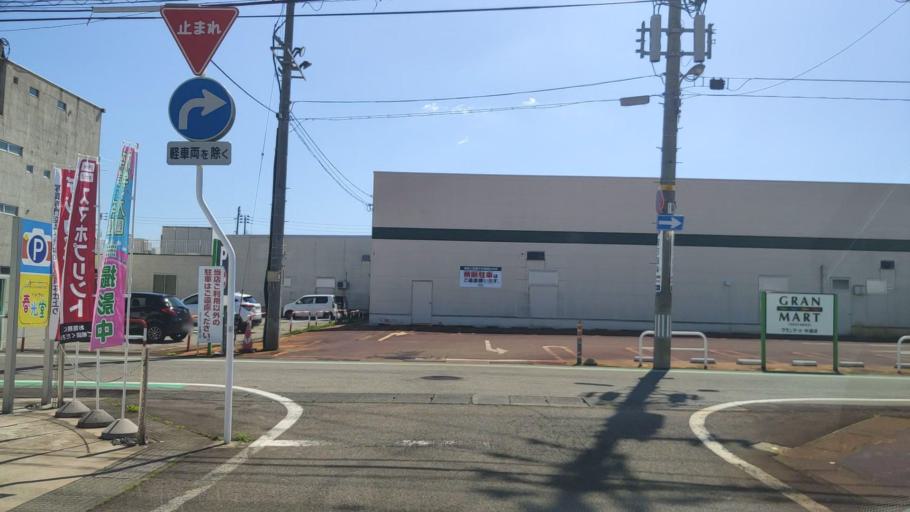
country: JP
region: Akita
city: Omagari
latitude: 39.4626
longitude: 140.4786
